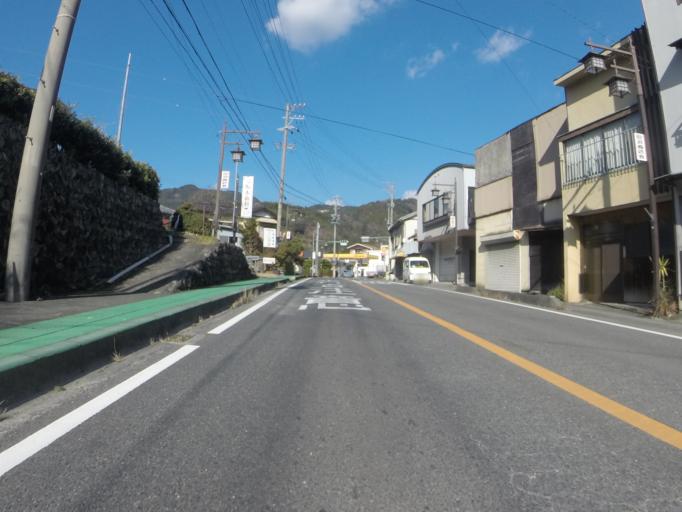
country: JP
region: Shizuoka
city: Fujinomiya
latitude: 35.0973
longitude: 138.5127
